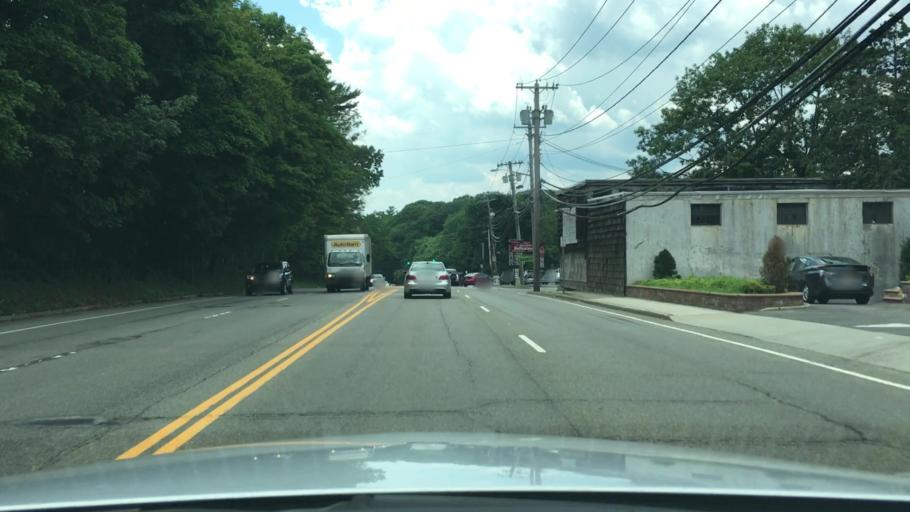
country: US
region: New York
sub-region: Suffolk County
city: West Hills
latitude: 40.8276
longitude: -73.4364
